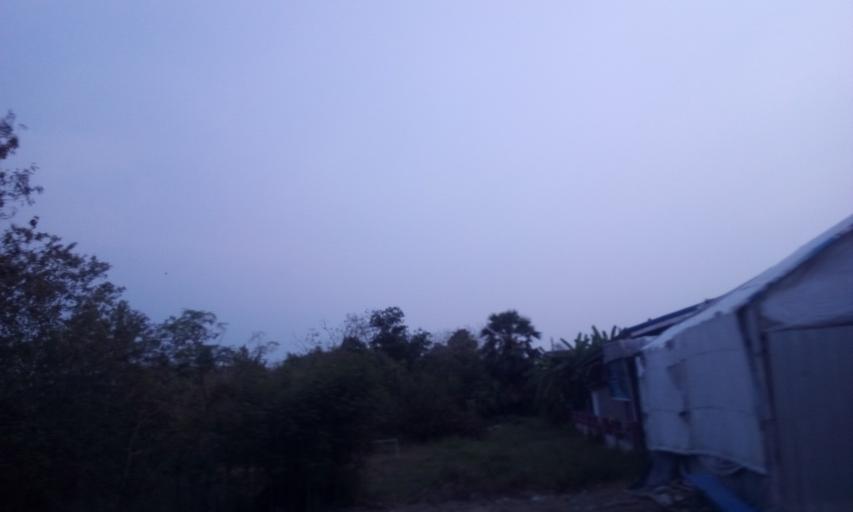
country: TH
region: Bangkok
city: Nong Chok
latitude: 13.8555
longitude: 100.8782
